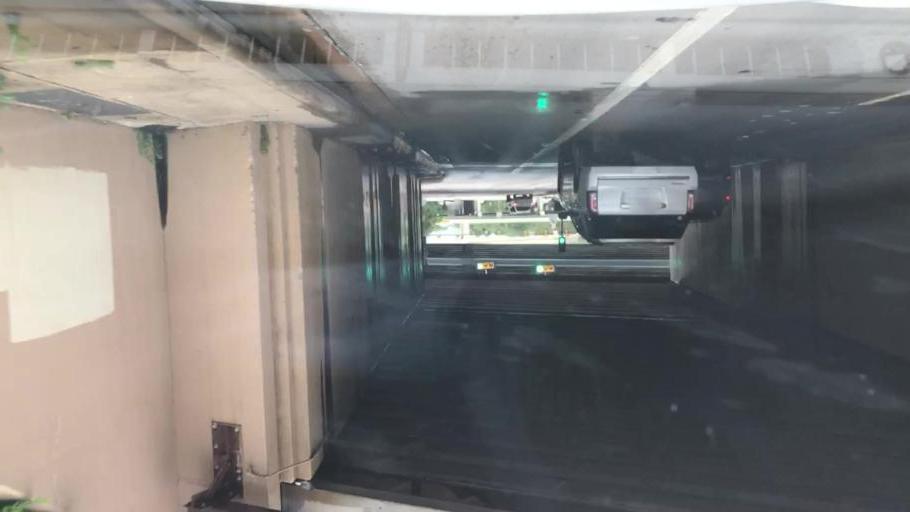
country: US
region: Texas
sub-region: Tarrant County
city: Fort Worth
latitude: 32.7313
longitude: -97.3613
